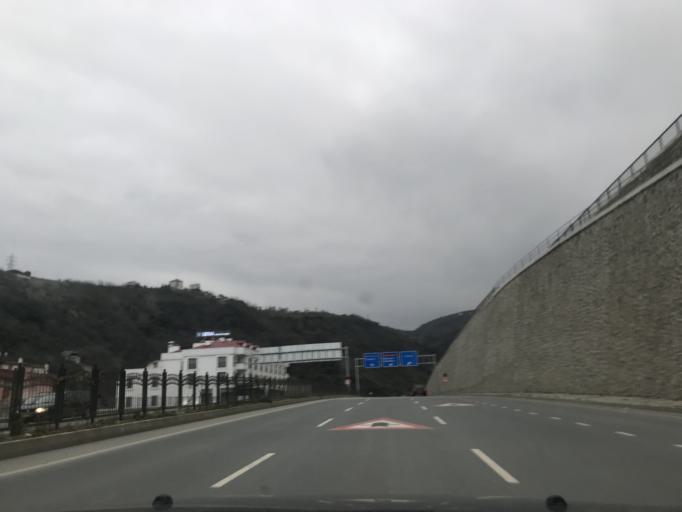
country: TR
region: Trabzon
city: Akcaabat
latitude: 41.0030
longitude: 39.6269
